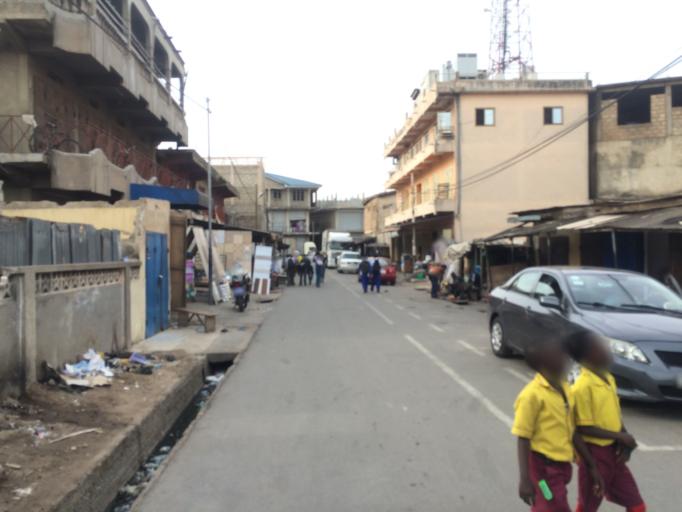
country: GH
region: Greater Accra
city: Accra
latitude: 5.5471
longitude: -0.2145
